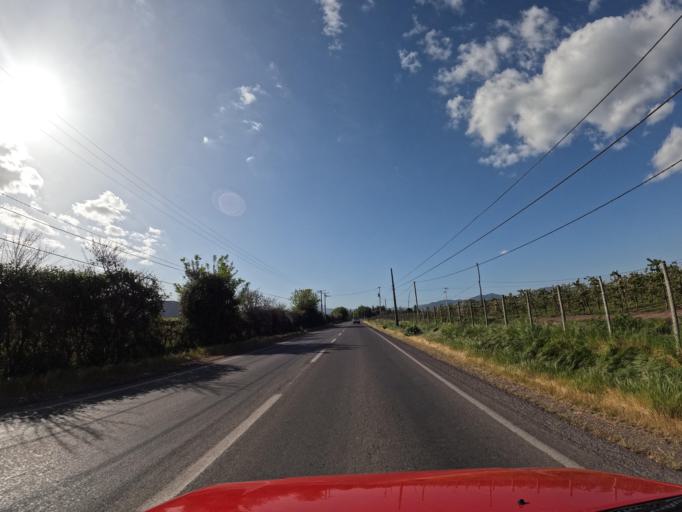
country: CL
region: Maule
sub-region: Provincia de Curico
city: Rauco
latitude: -34.9122
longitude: -71.2779
